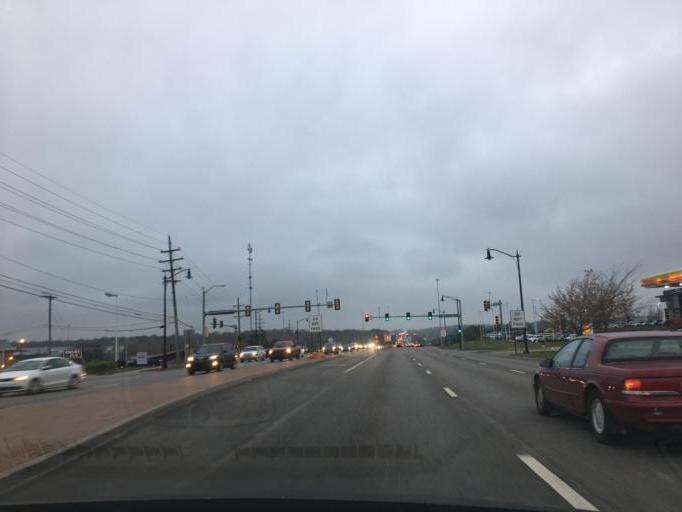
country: US
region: Kansas
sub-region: Johnson County
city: Merriam
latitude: 39.0150
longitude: -94.6886
